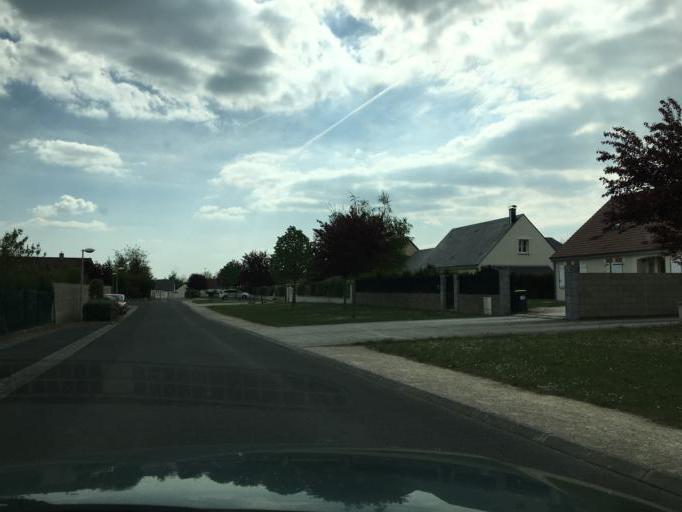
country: FR
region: Centre
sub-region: Departement du Loiret
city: Beaugency
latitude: 47.7936
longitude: 1.6313
